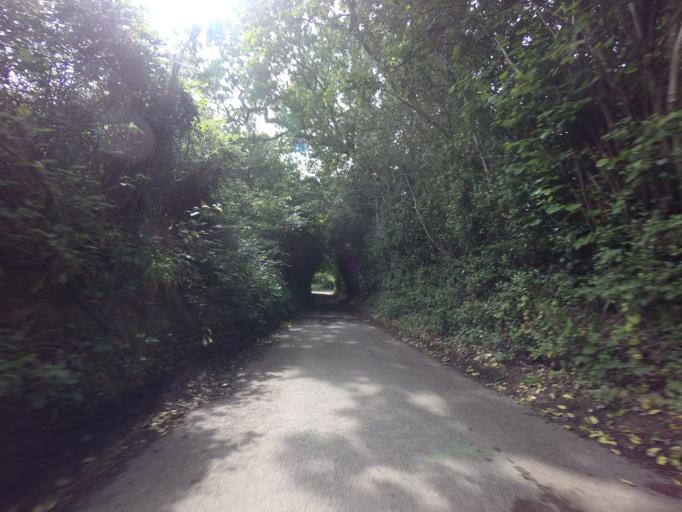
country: GB
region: England
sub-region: Kent
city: Halstead
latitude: 51.3503
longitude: 0.1409
